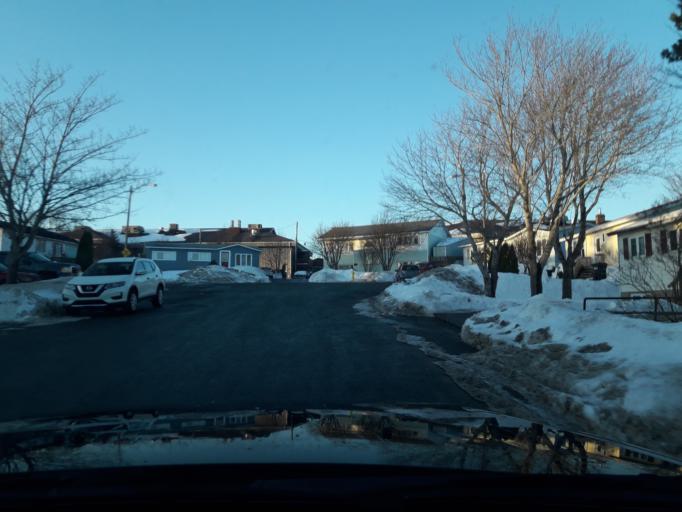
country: CA
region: Newfoundland and Labrador
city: Mount Pearl
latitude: 47.5235
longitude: -52.7697
